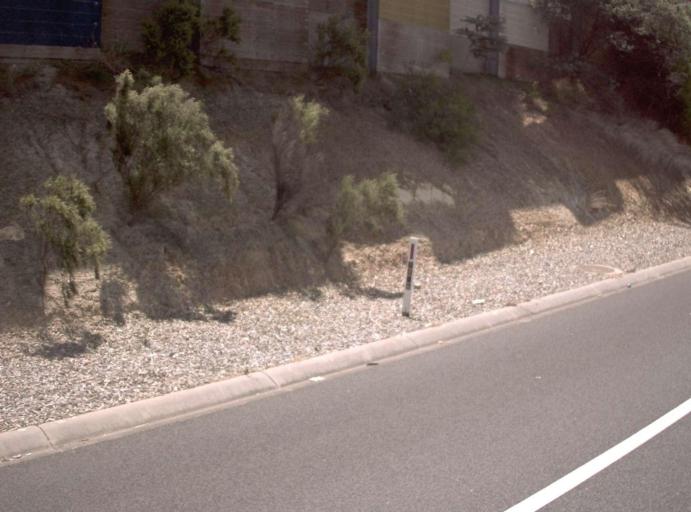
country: AU
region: Victoria
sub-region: Manningham
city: Donvale
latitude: -37.8030
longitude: 145.1825
